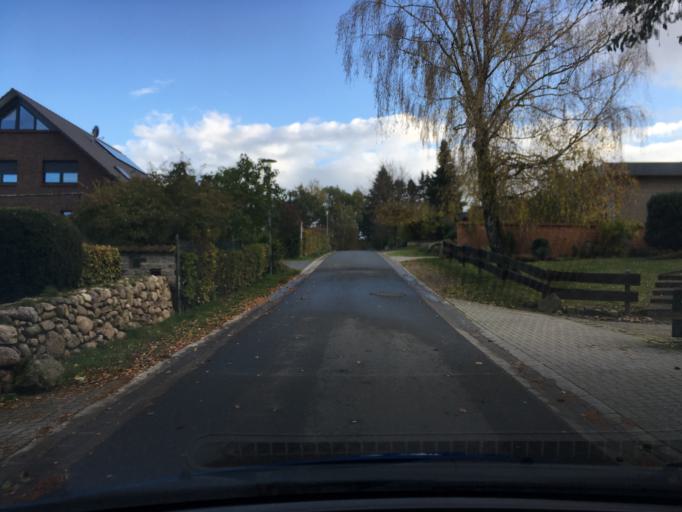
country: DE
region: Lower Saxony
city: Reinstorf
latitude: 53.2475
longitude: 10.5577
